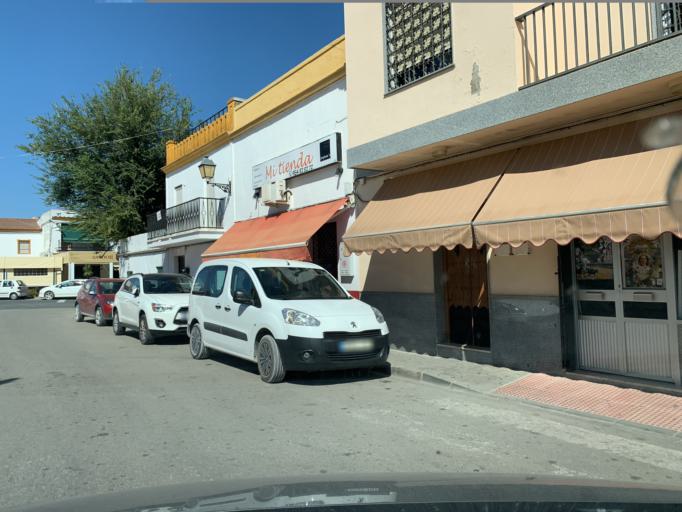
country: ES
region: Andalusia
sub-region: Provincia de Sevilla
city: La Lantejuela
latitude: 37.3546
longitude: -5.2250
